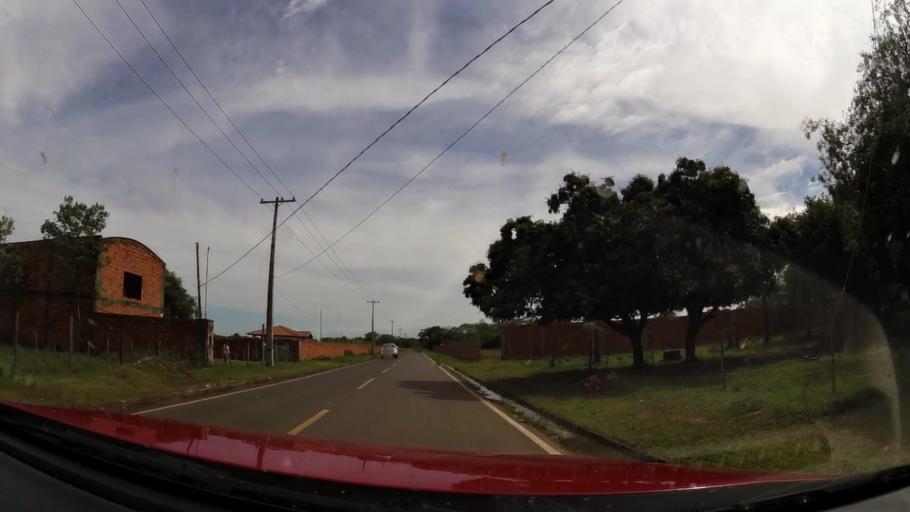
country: PY
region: Central
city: Limpio
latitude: -25.1819
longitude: -57.4737
